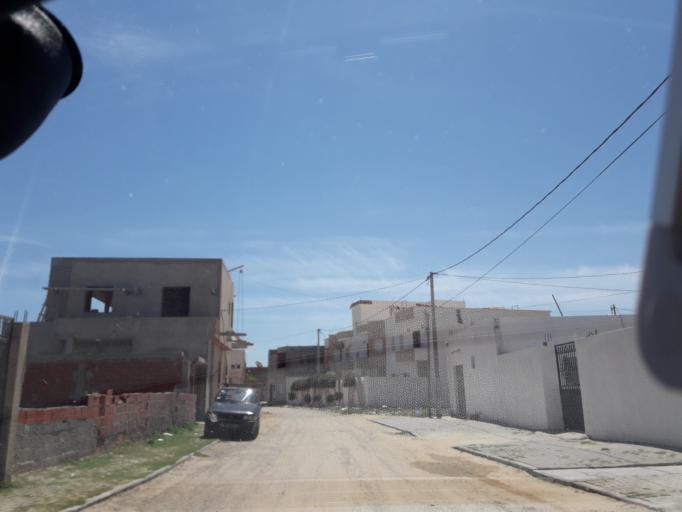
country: TN
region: Safaqis
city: Sfax
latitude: 34.7414
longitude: 10.5221
